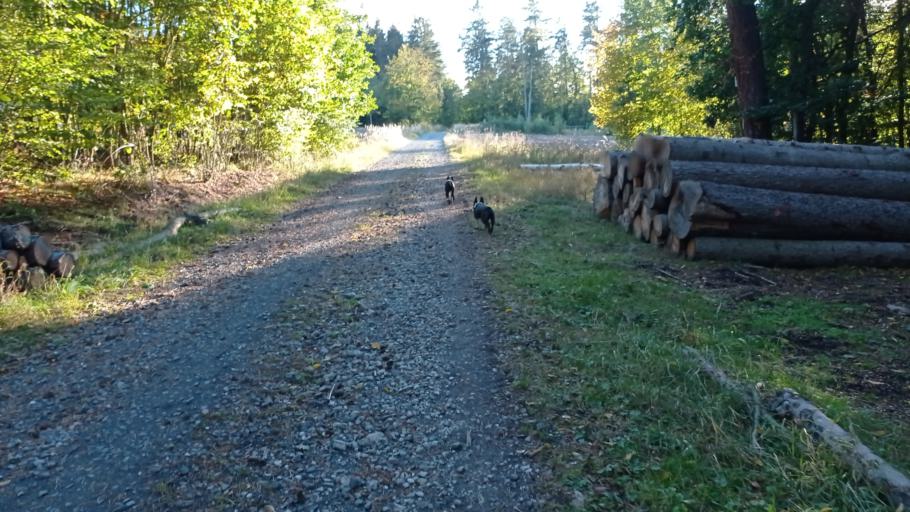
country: CZ
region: Central Bohemia
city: Chynava
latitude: 50.0599
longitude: 14.0551
